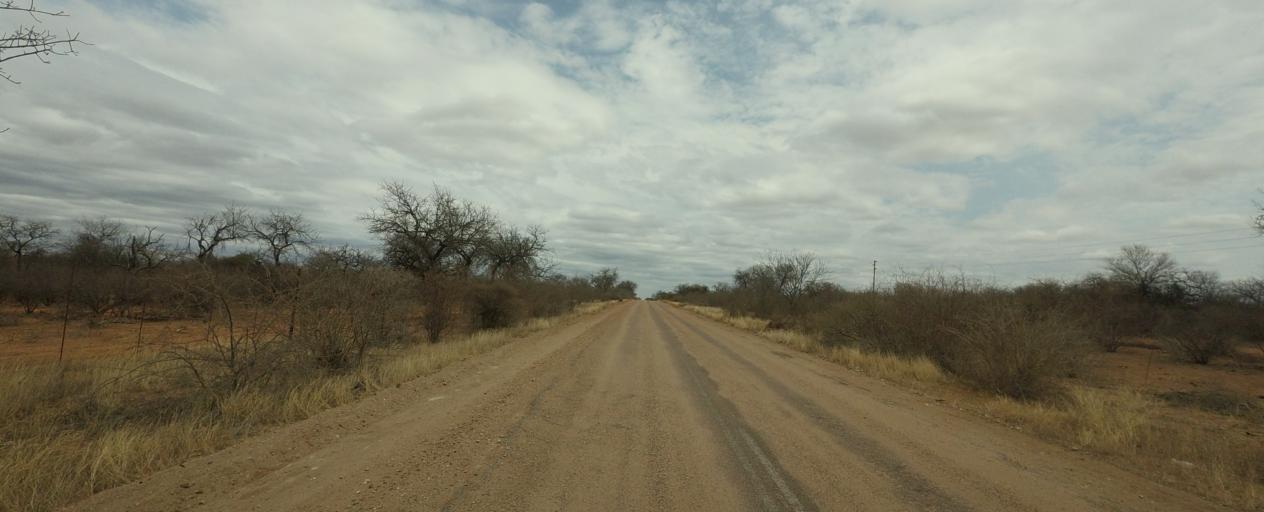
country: BW
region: Central
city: Mathathane
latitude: -22.6713
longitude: 28.6819
